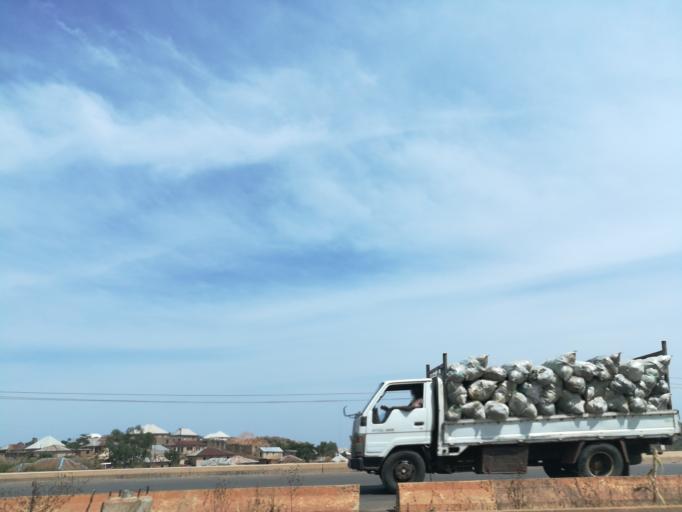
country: NG
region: Plateau
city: Bukuru
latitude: 9.8345
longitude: 8.8669
